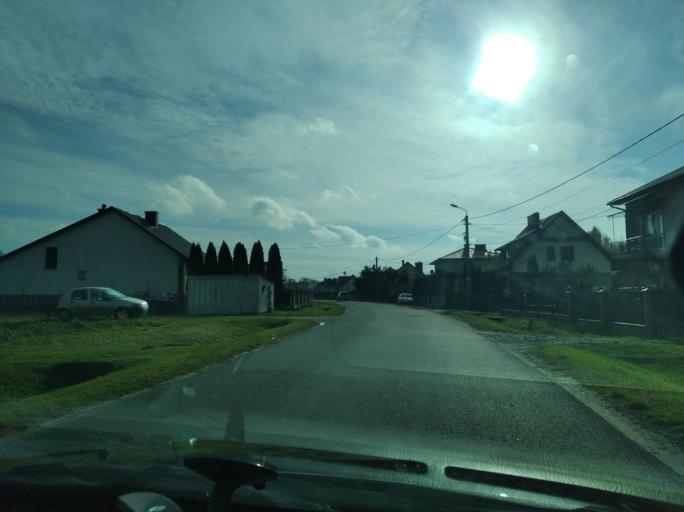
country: PL
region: Subcarpathian Voivodeship
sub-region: Powiat ropczycko-sedziszowski
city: Sedziszow Malopolski
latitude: 50.1049
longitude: 21.7330
